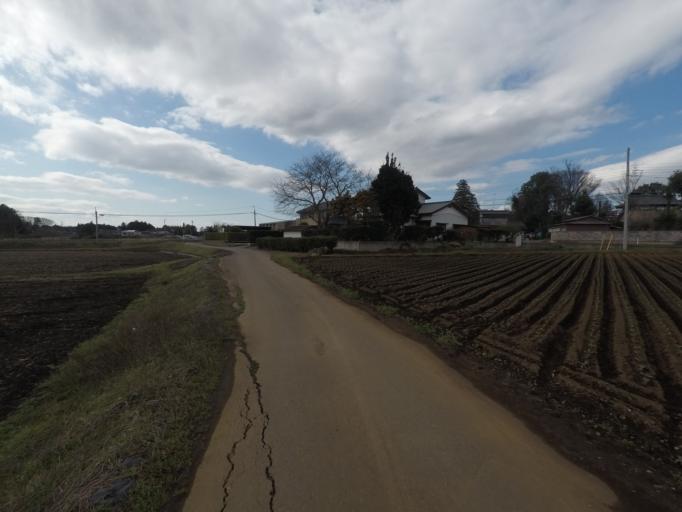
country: JP
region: Ibaraki
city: Ushiku
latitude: 36.0170
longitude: 140.1090
